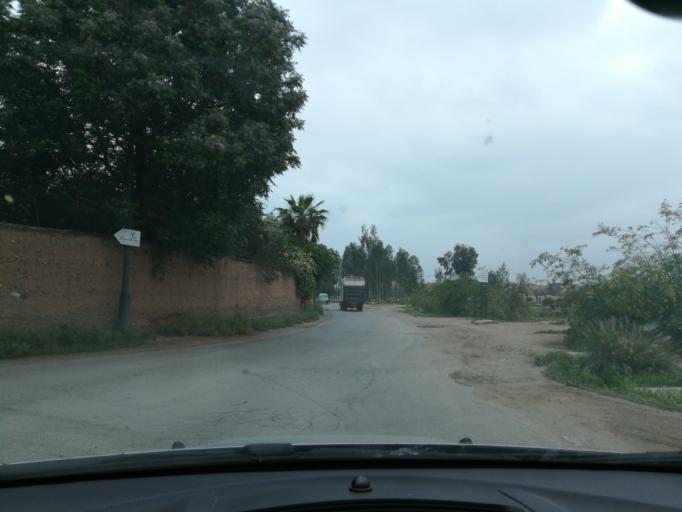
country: MA
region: Marrakech-Tensift-Al Haouz
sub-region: Marrakech
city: Marrakesh
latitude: 31.6601
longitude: -7.9829
